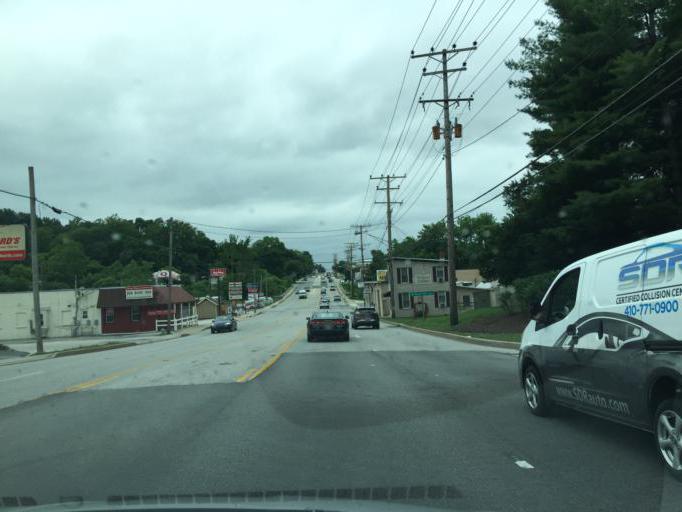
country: US
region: Maryland
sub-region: Baltimore County
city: Cockeysville
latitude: 39.4874
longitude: -76.6467
